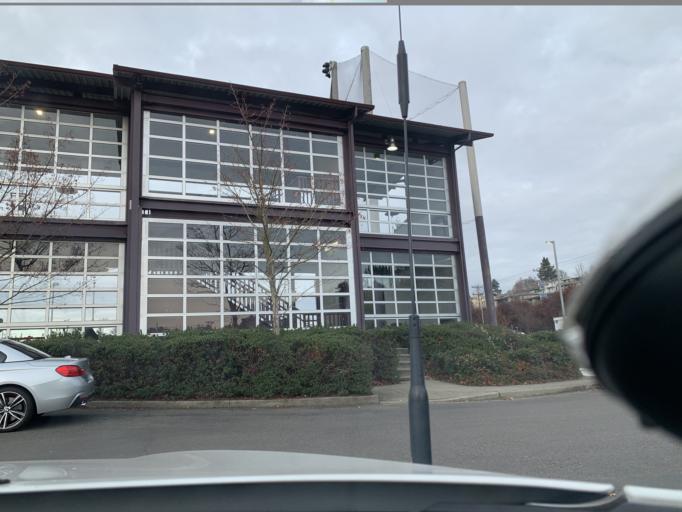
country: US
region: Washington
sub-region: King County
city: Seattle
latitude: 47.6442
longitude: -122.3772
